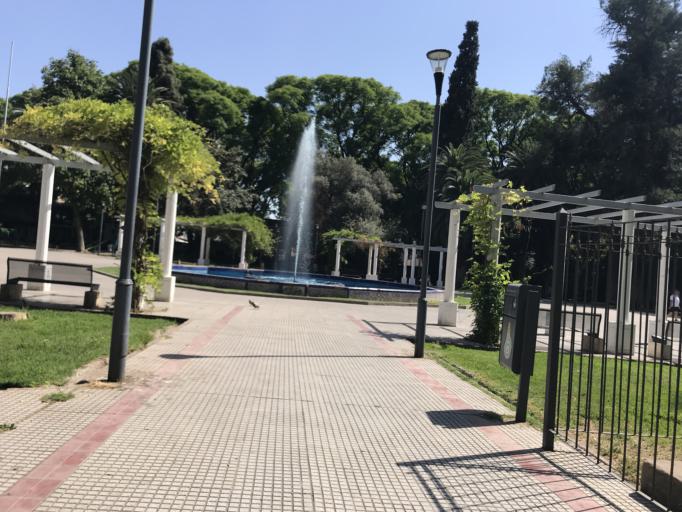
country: AR
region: Mendoza
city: Mendoza
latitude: -32.8920
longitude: -68.8485
